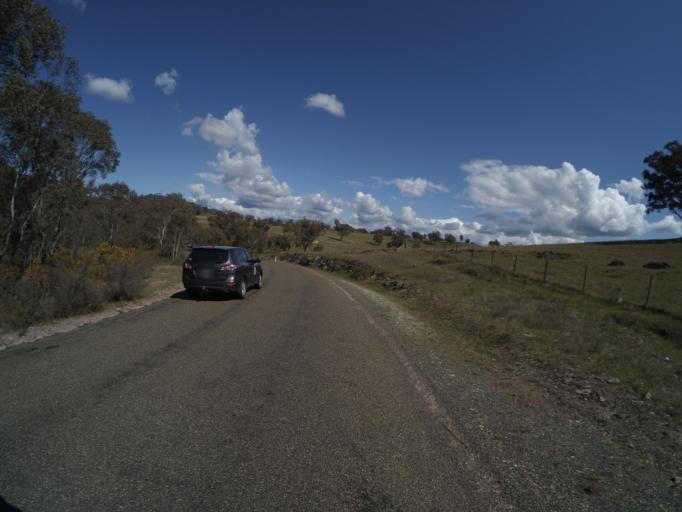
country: AU
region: New South Wales
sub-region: Yass Valley
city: Murrumbateman
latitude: -35.0665
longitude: 148.8358
